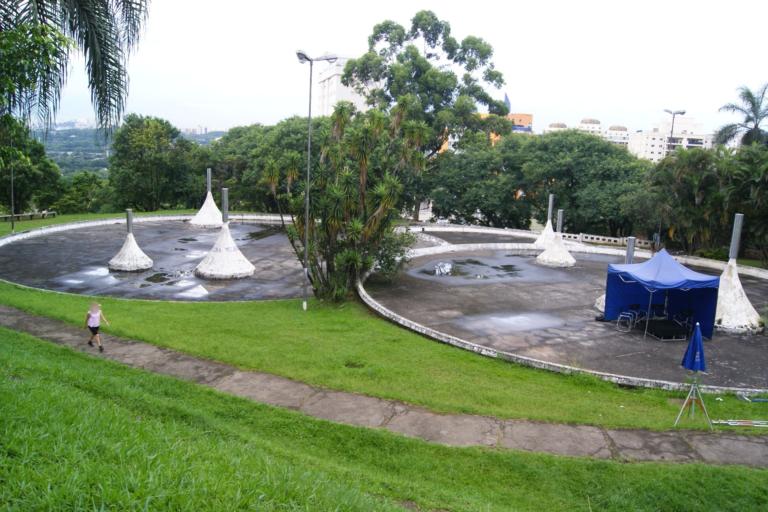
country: BR
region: Sao Paulo
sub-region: Sao Paulo
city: Sao Paulo
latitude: -23.5381
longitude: -46.7119
